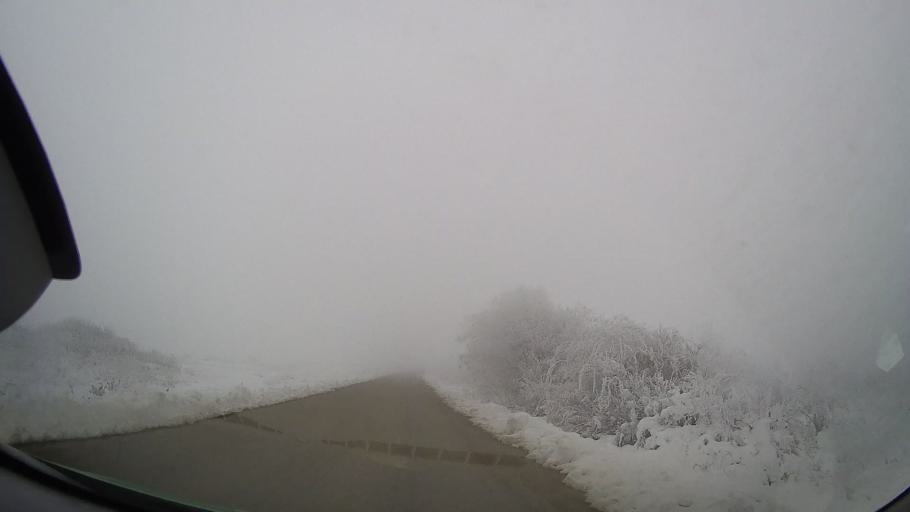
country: RO
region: Iasi
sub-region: Comuna Tansa
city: Suhulet
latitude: 46.8900
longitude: 27.2693
